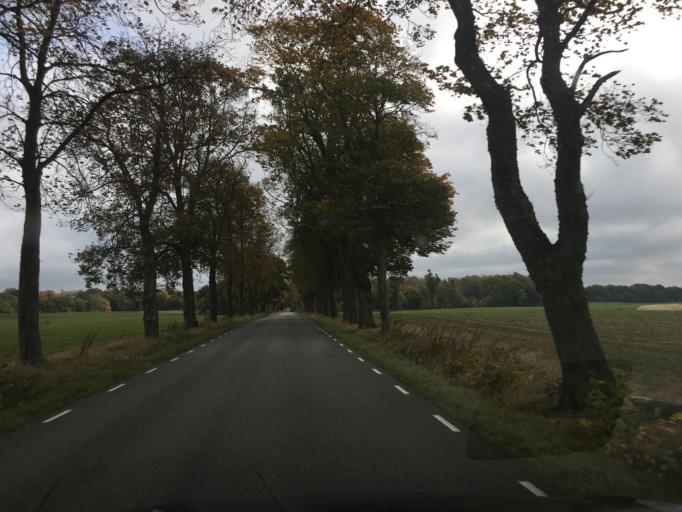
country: SE
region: Skane
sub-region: Tomelilla Kommun
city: Tomelilla
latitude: 55.6470
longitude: 14.0388
